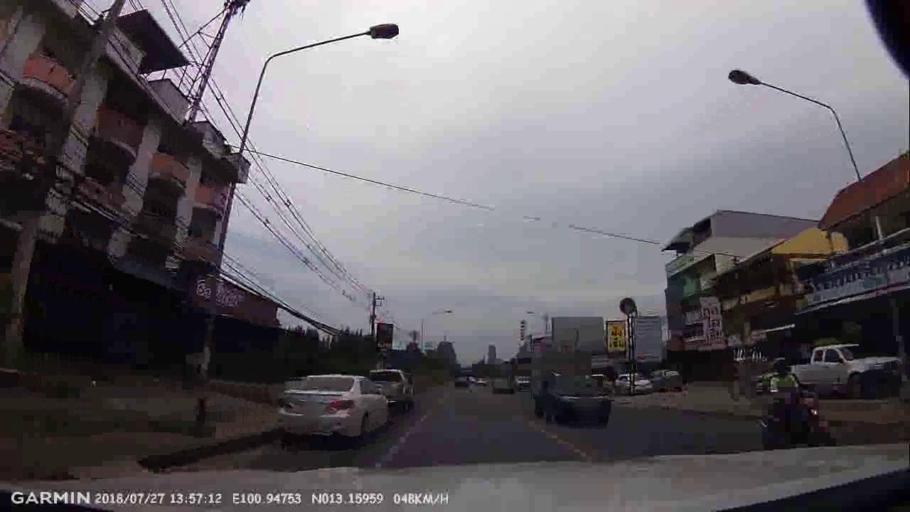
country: TH
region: Chon Buri
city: Si Racha
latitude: 13.1596
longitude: 100.9475
